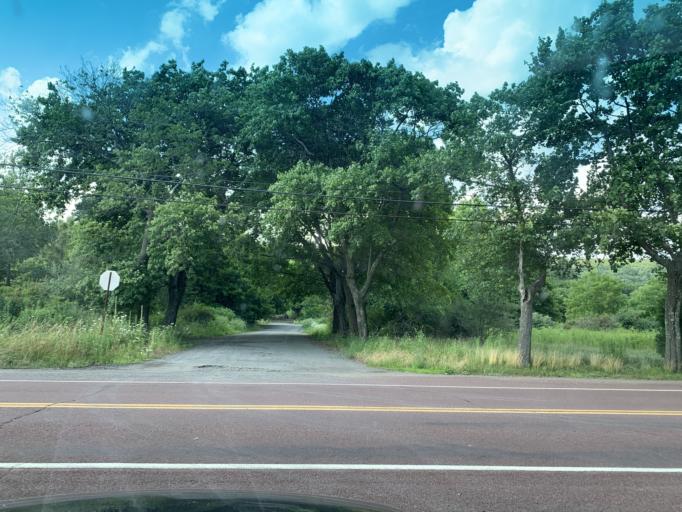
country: US
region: Pennsylvania
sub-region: Schuylkill County
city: Ashland
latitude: 40.8040
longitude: -76.3422
